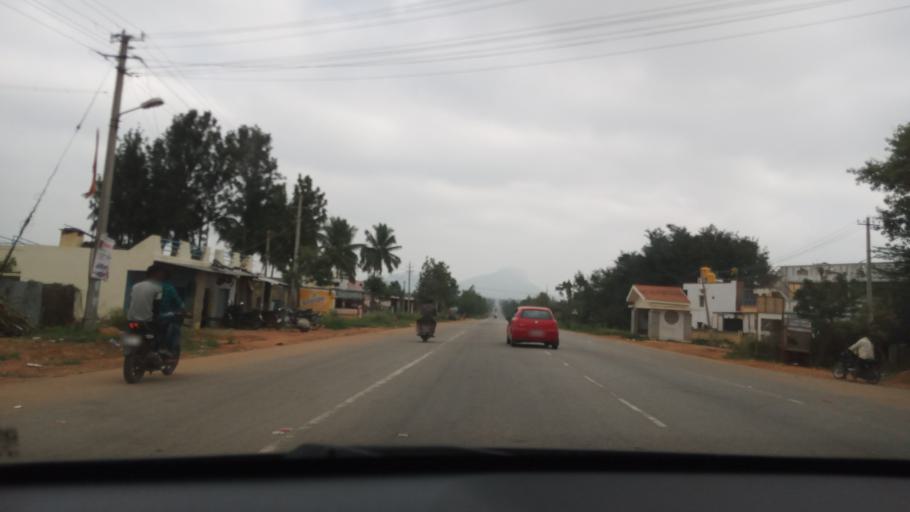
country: IN
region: Karnataka
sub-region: Chikkaballapur
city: Chintamani
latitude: 13.2932
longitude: 77.9656
